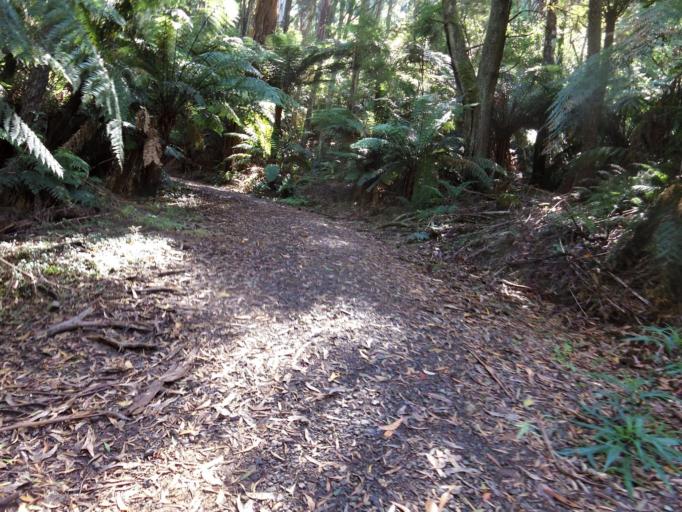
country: AU
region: Victoria
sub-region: Yarra Ranges
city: Olinda
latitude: -37.8497
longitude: 145.3571
